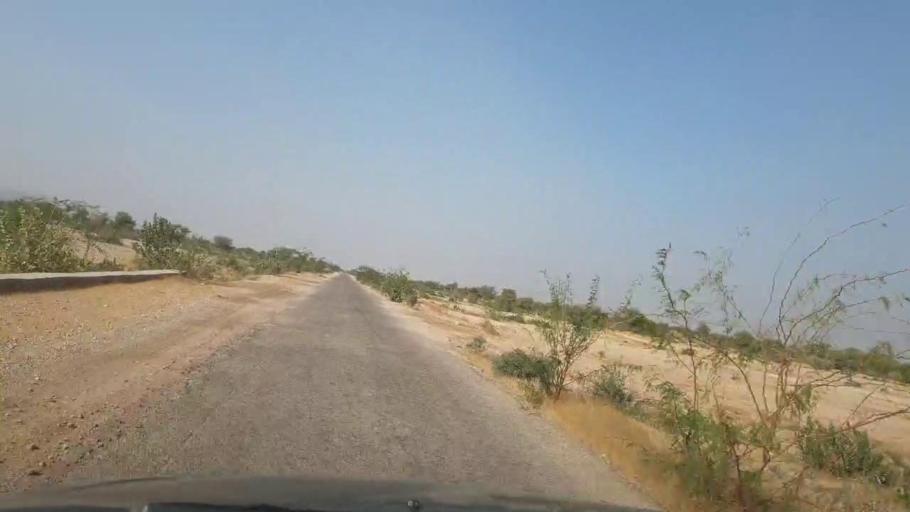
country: PK
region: Sindh
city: Jamshoro
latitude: 25.5545
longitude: 67.8289
